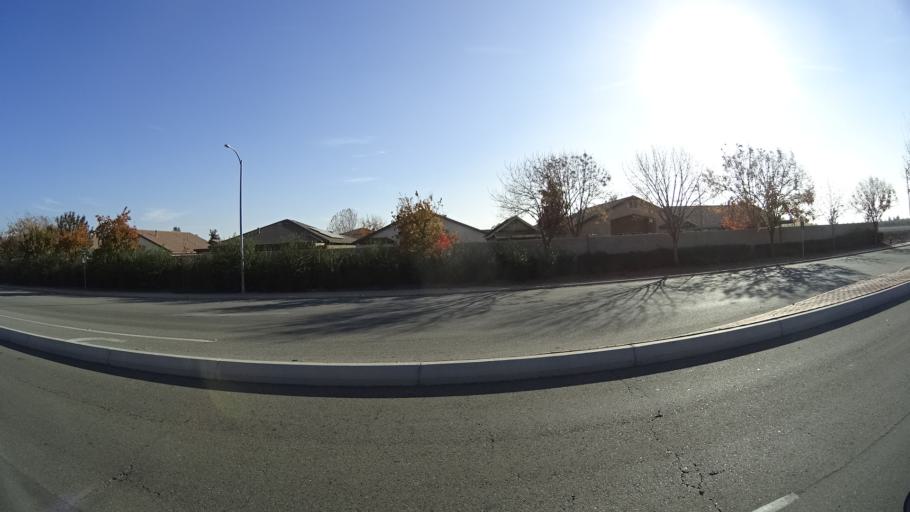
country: US
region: California
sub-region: Kern County
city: Greenacres
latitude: 35.2963
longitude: -119.1225
